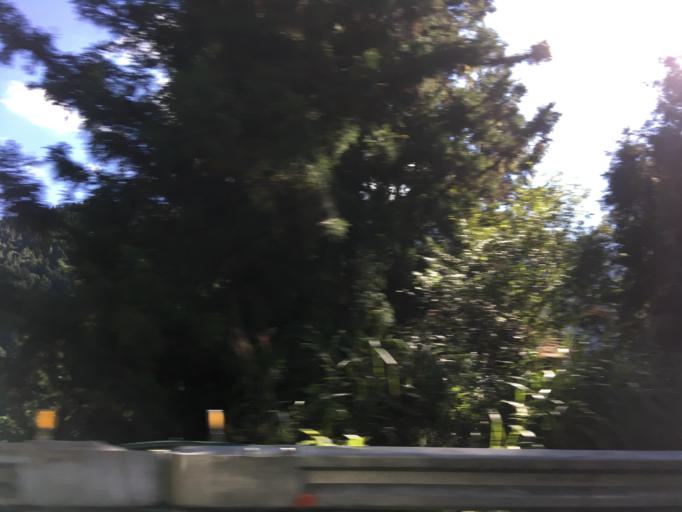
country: TW
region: Taiwan
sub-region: Yilan
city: Yilan
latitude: 24.5027
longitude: 121.5536
